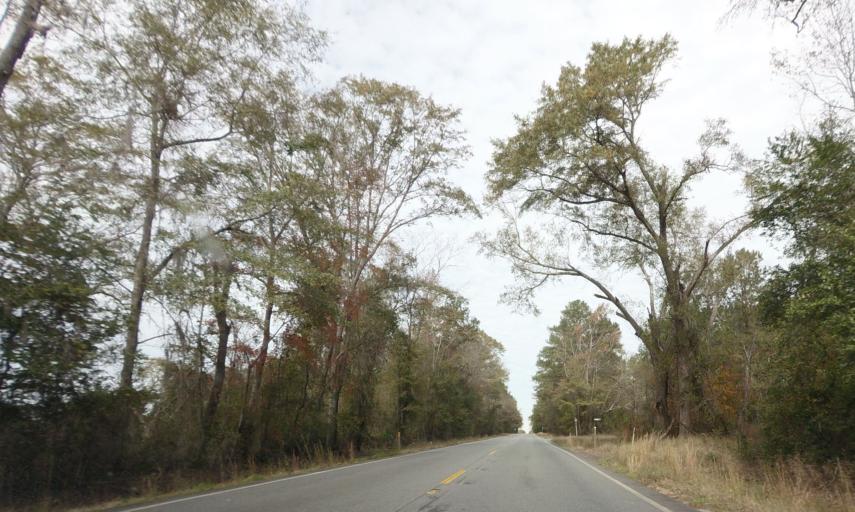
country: US
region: Georgia
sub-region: Dodge County
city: Chester
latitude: 32.5047
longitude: -83.0925
